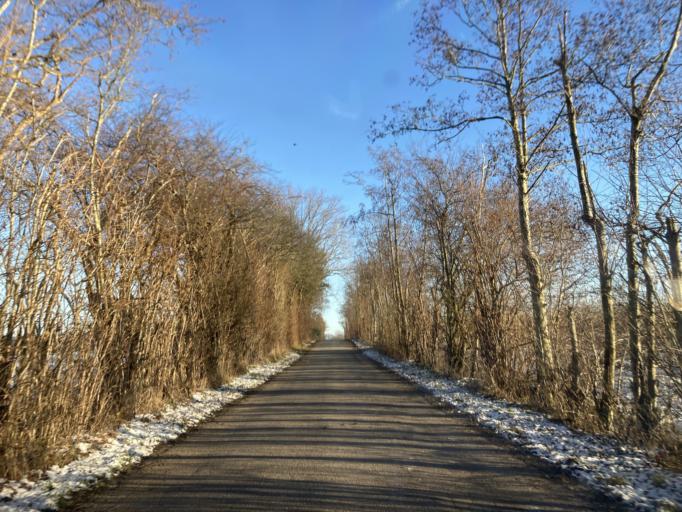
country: DK
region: South Denmark
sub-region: Svendborg Kommune
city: Thuro By
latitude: 55.1485
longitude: 10.7271
